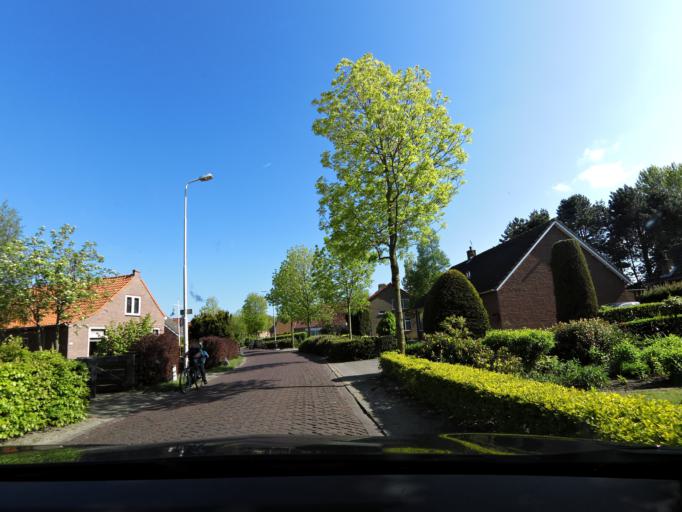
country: NL
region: South Holland
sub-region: Gemeente Goeree-Overflakkee
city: Ouddorp
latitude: 51.8020
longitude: 3.9329
